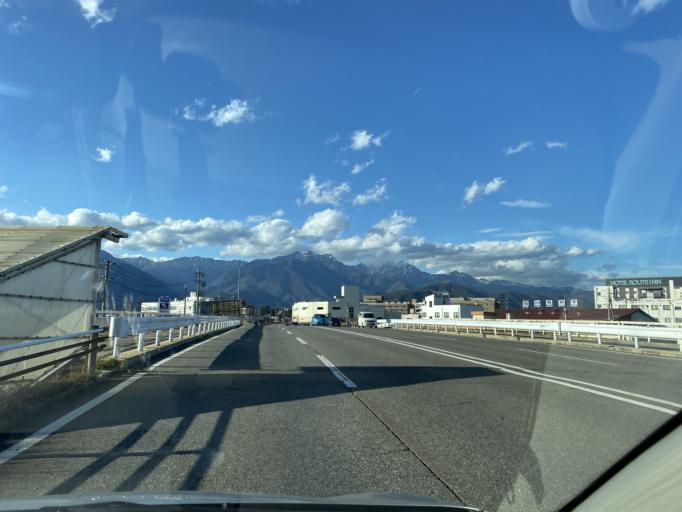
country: JP
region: Nagano
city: Omachi
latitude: 36.4977
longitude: 137.8606
